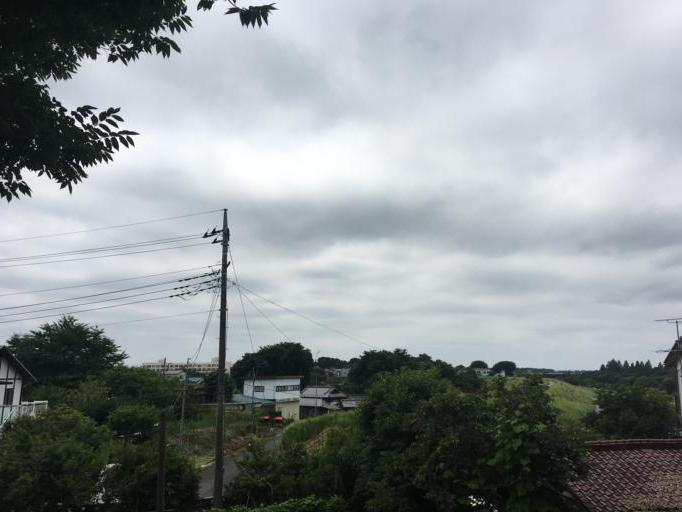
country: JP
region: Saitama
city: Okegawa
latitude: 35.9515
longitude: 139.5461
